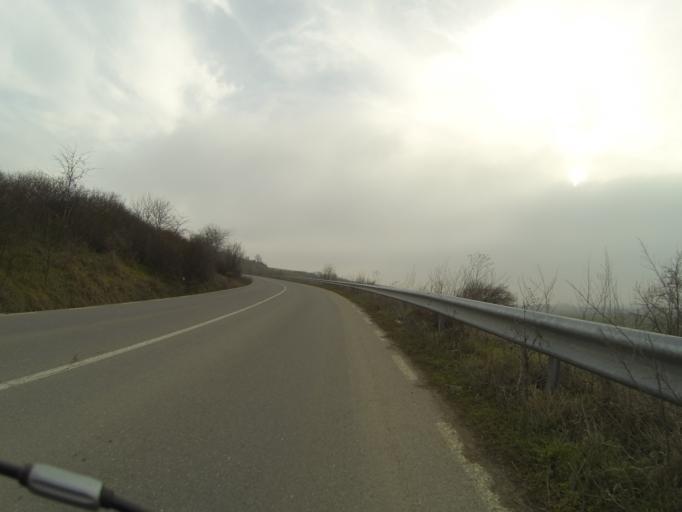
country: RO
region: Mehedinti
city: Vanju-Mare
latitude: 44.4157
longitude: 22.8764
